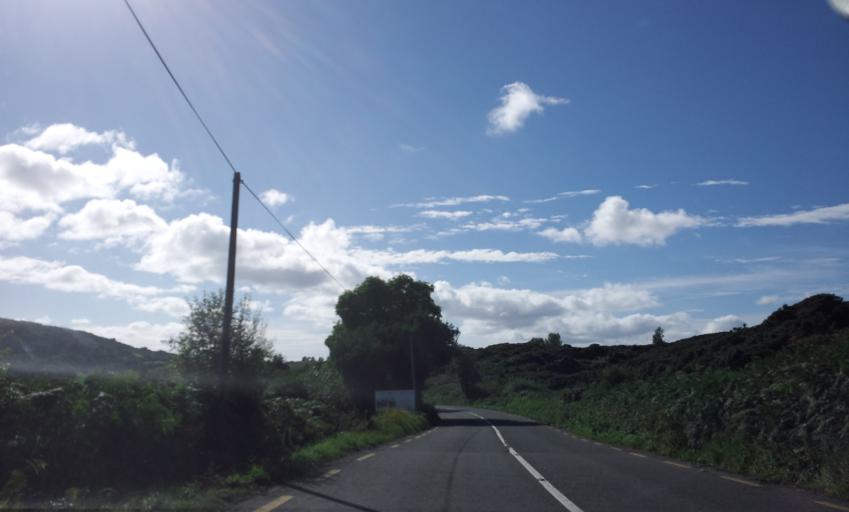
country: IE
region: Munster
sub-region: County Cork
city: Millstreet
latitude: 51.9247
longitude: -9.1106
